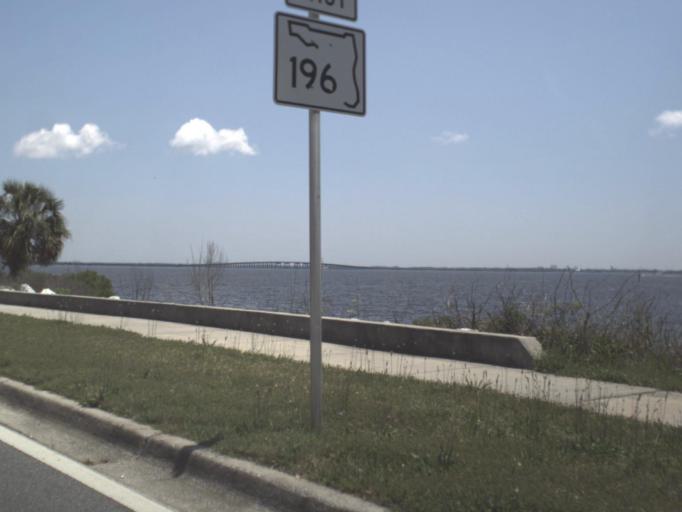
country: US
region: Florida
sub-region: Escambia County
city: Pensacola
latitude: 30.4083
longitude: -87.2084
